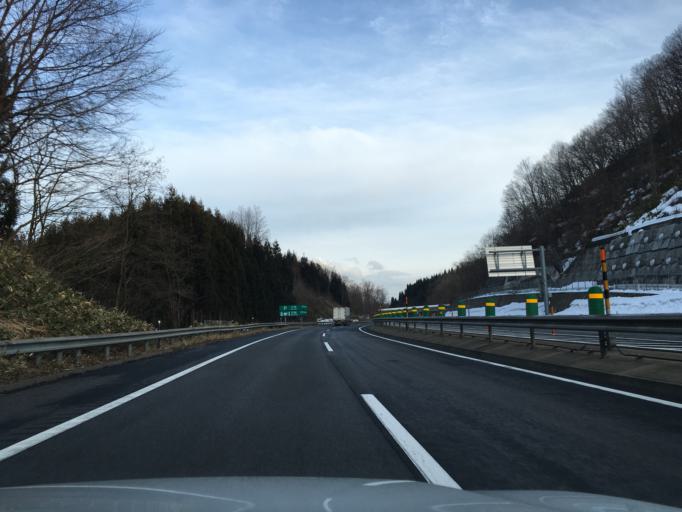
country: JP
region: Akita
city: Odate
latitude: 40.3679
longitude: 140.7186
